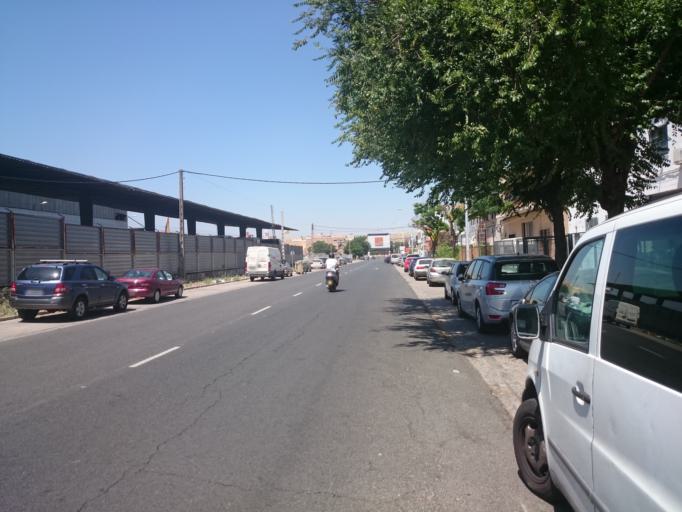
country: ES
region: Andalusia
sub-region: Provincia de Sevilla
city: Sevilla
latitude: 37.3885
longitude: -5.9547
